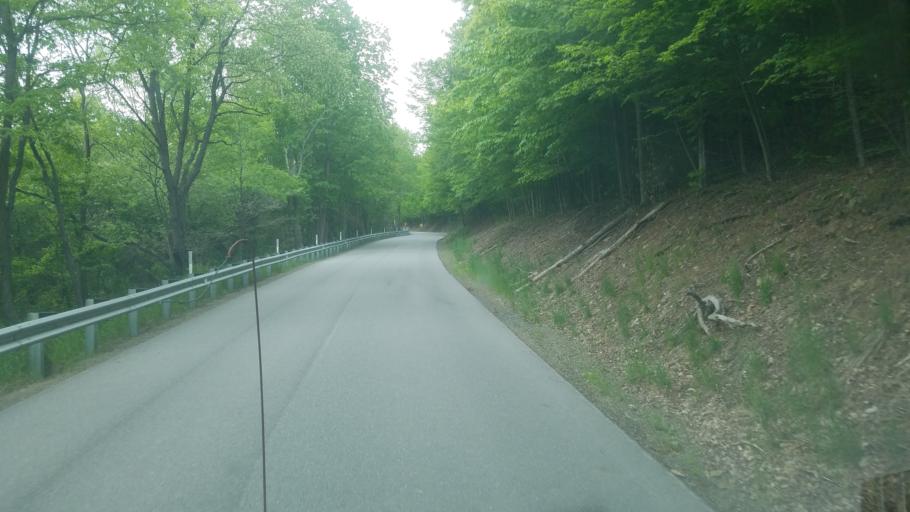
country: US
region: Pennsylvania
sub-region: Tioga County
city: Westfield
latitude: 41.8313
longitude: -77.5892
